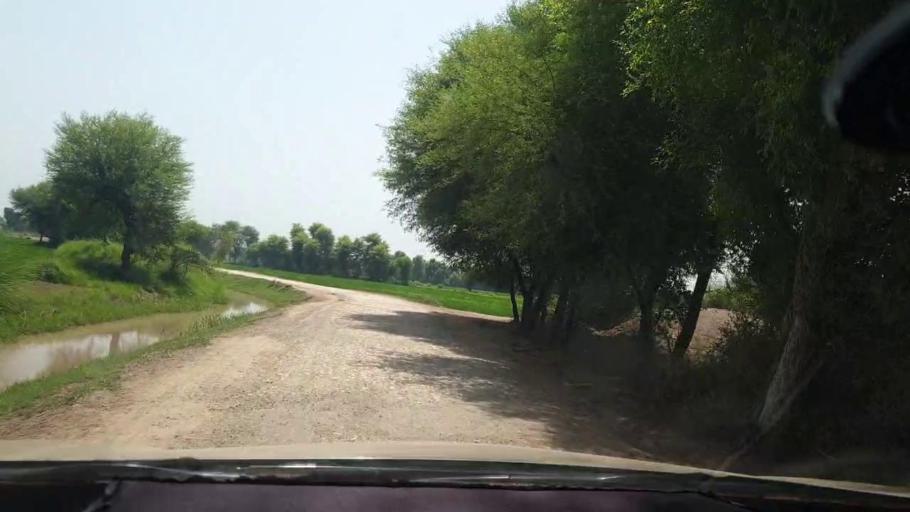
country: PK
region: Sindh
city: Kambar
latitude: 27.6679
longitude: 67.9432
